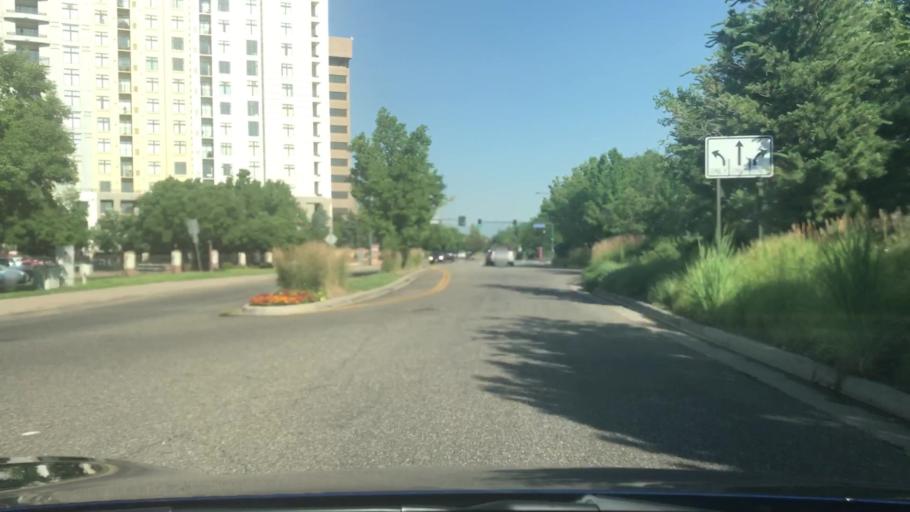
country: US
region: Colorado
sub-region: Arapahoe County
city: Glendale
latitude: 39.7037
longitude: -104.9328
